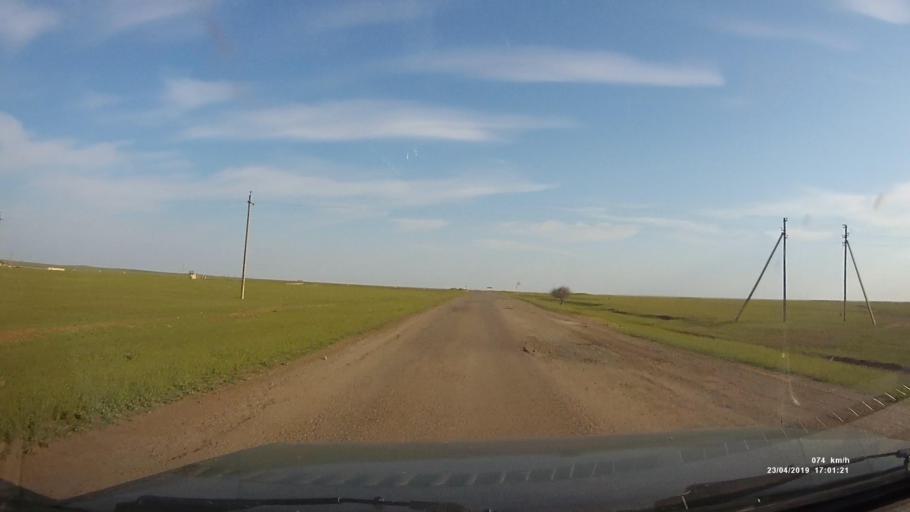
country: RU
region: Kalmykiya
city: Priyutnoye
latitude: 46.2971
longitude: 43.4077
